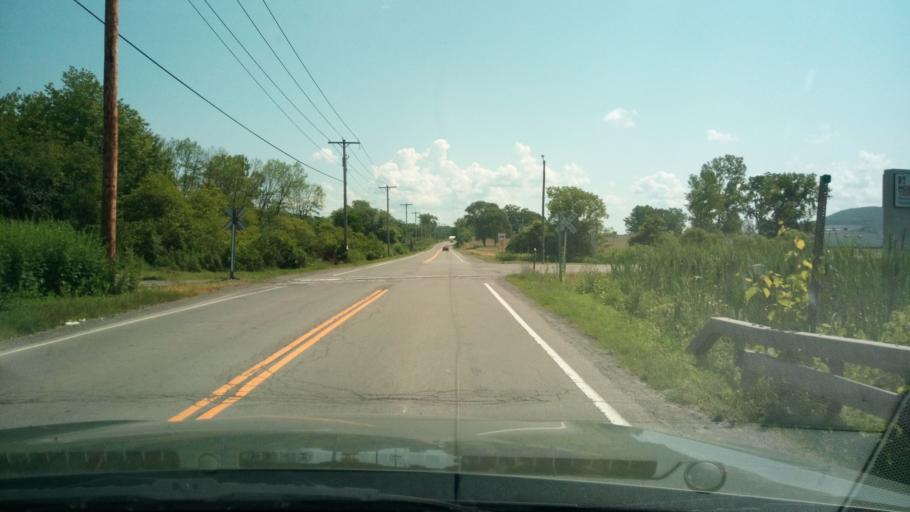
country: US
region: New York
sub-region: Chemung County
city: Horseheads North
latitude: 42.1896
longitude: -76.8320
